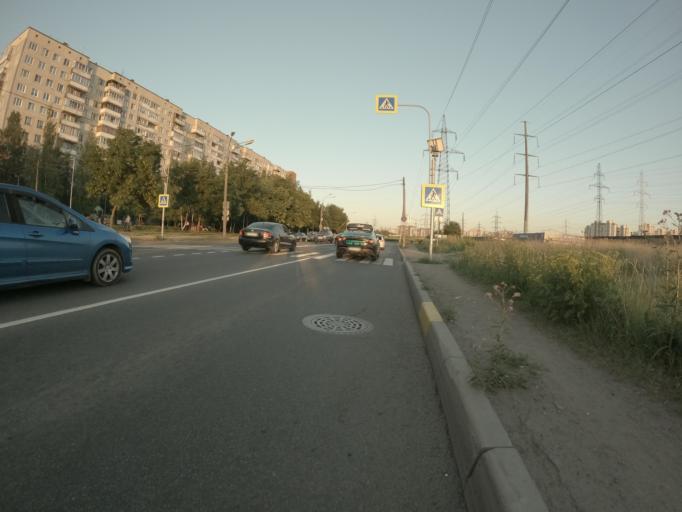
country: RU
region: St.-Petersburg
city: Krasnogvargeisky
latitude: 59.9395
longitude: 30.4678
